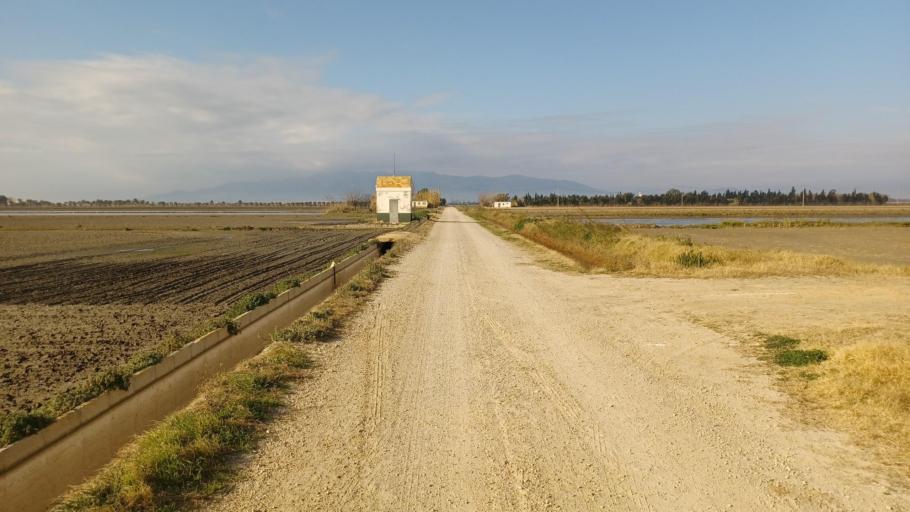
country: ES
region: Catalonia
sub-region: Provincia de Tarragona
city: Deltebre
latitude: 40.6425
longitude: 0.7045
